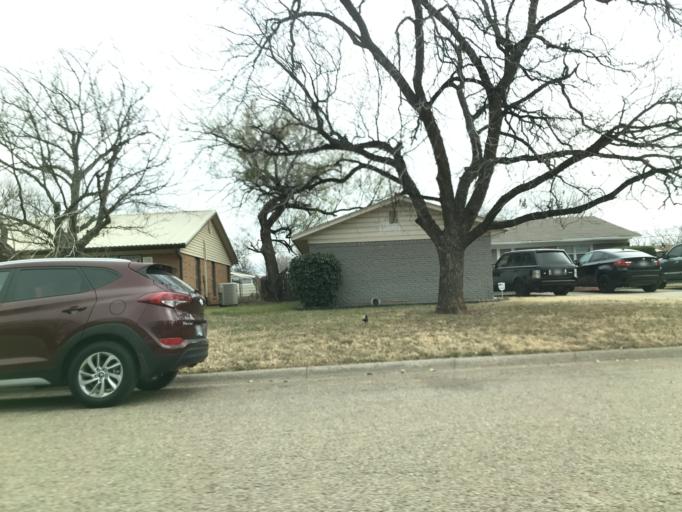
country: US
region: Texas
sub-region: Taylor County
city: Abilene
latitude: 32.4723
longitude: -99.7621
